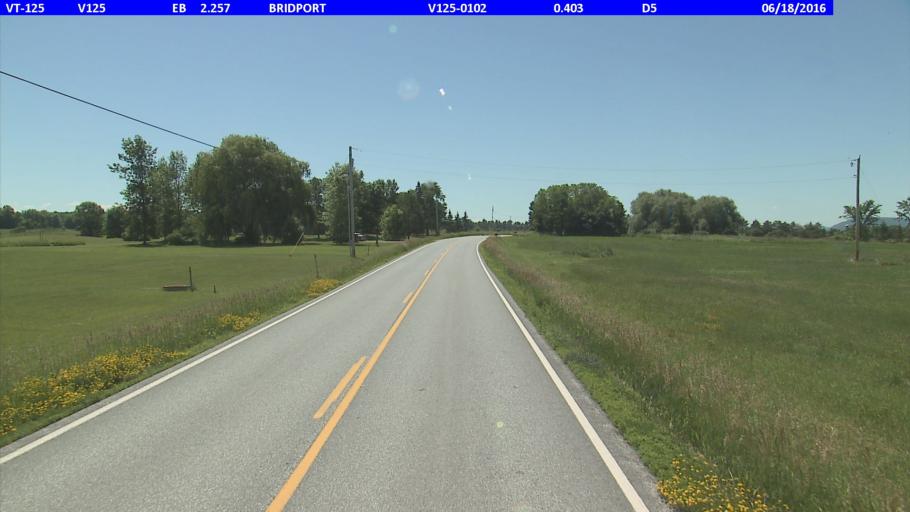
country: US
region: New York
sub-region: Essex County
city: Port Henry
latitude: 44.0163
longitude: -73.3895
